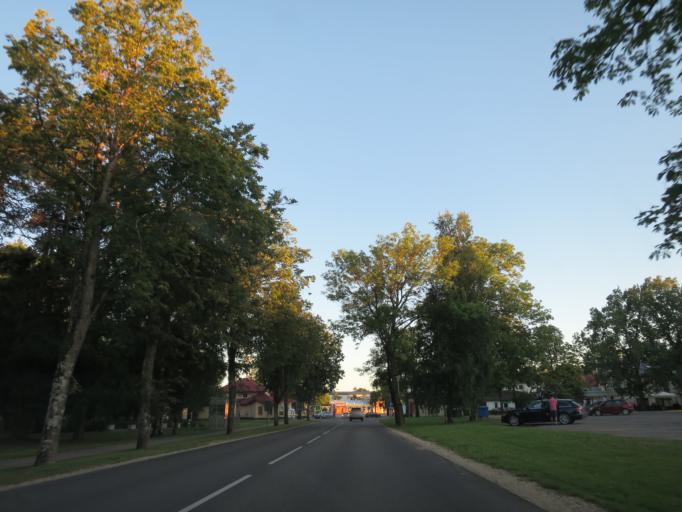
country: LV
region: Sigulda
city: Sigulda
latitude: 57.1555
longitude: 24.8543
